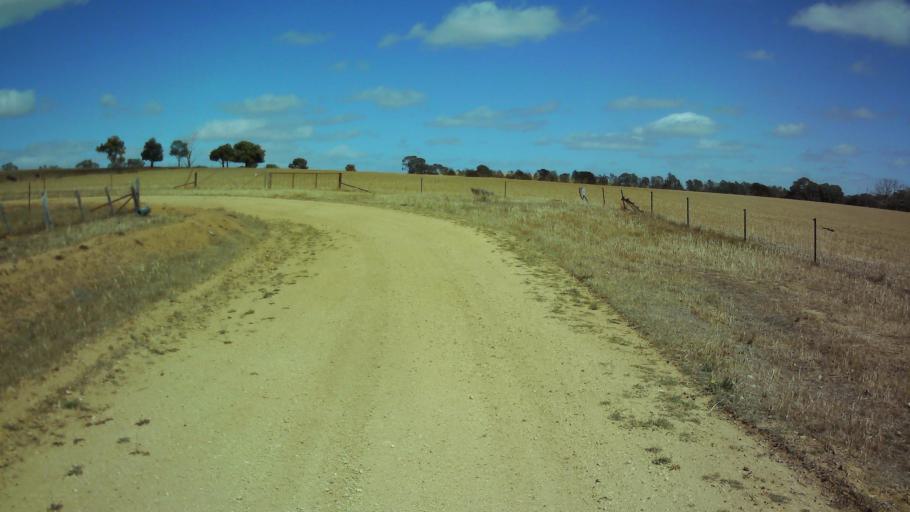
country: AU
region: New South Wales
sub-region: Weddin
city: Grenfell
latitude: -33.9795
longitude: 148.3884
